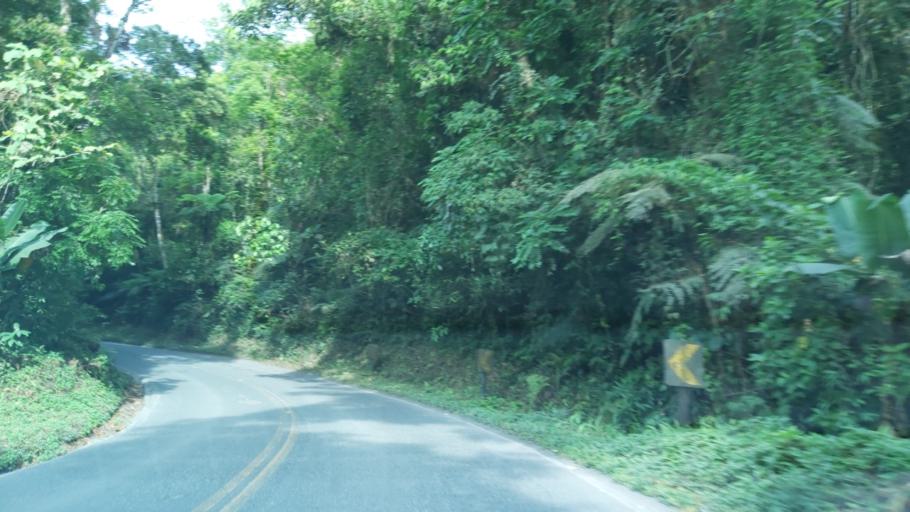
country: BR
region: Sao Paulo
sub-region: Juquia
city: Juquia
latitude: -24.1112
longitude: -47.6250
